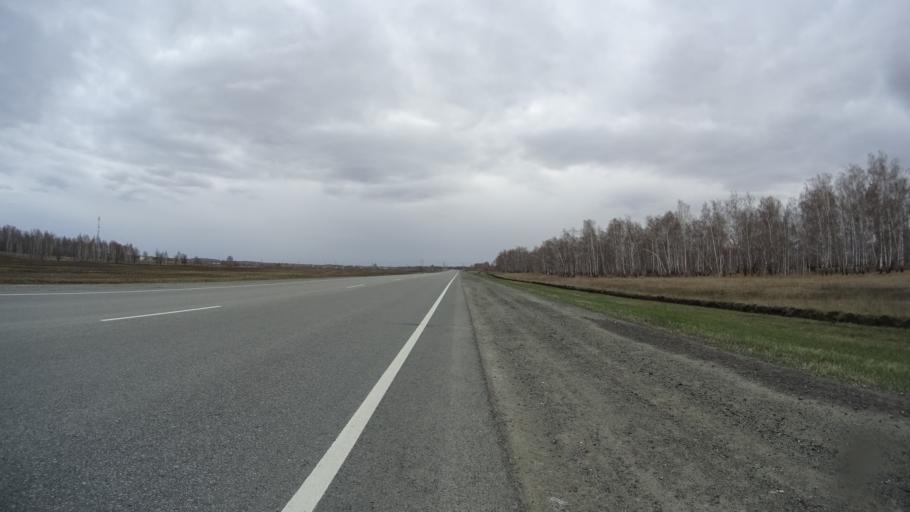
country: RU
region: Chelyabinsk
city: Krasnogorskiy
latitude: 54.6891
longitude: 61.2484
